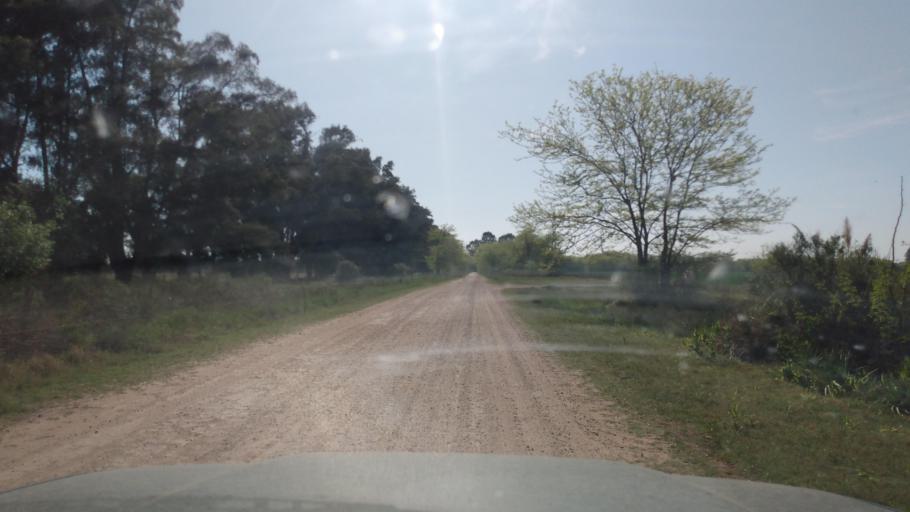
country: AR
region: Buenos Aires
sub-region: Partido de Lujan
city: Lujan
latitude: -34.6288
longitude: -59.1004
